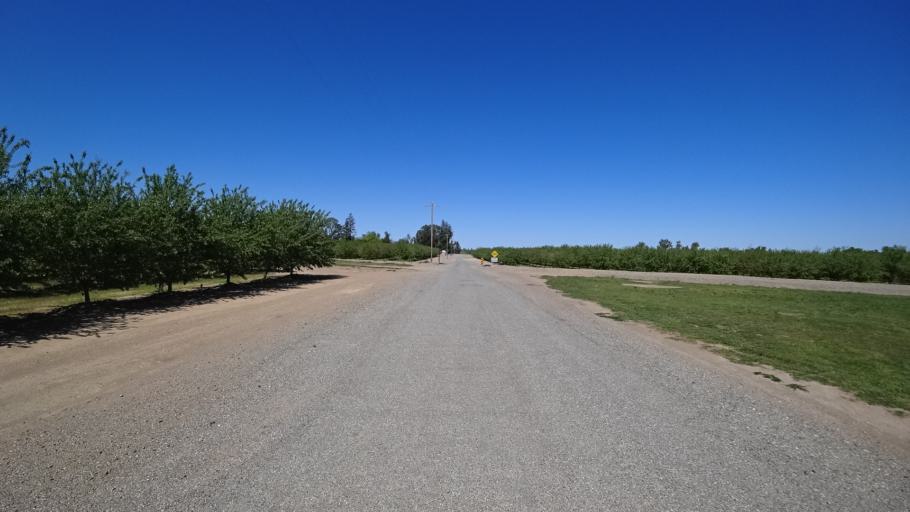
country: US
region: California
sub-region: Glenn County
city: Orland
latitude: 39.7545
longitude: -122.1598
